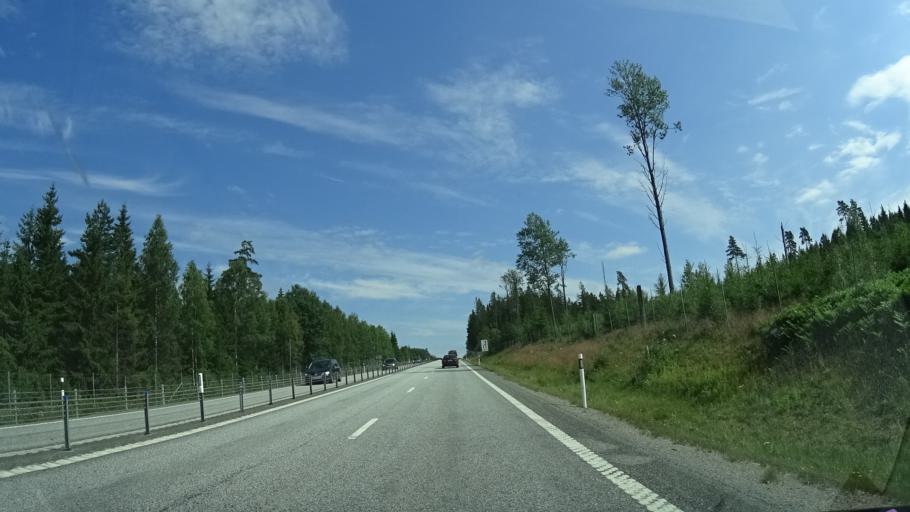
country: SE
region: Vaermland
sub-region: Kristinehamns Kommun
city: Bjorneborg
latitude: 59.3155
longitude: 14.3316
